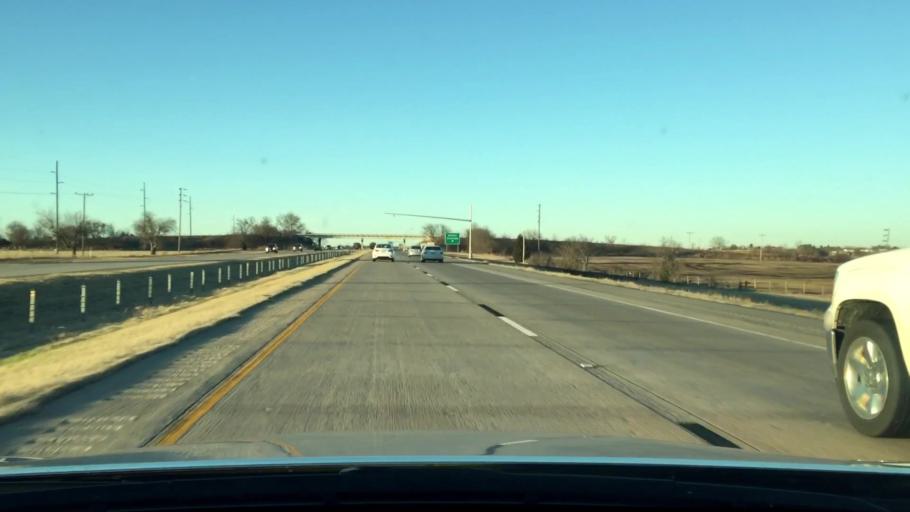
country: US
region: Oklahoma
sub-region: Love County
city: Marietta
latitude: 33.8934
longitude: -97.1344
